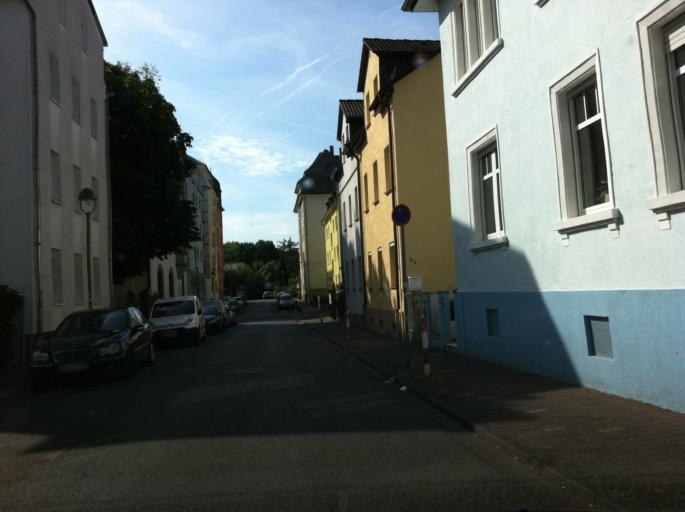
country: DE
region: Hesse
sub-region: Regierungsbezirk Darmstadt
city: Eschborn
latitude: 50.1246
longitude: 8.6095
